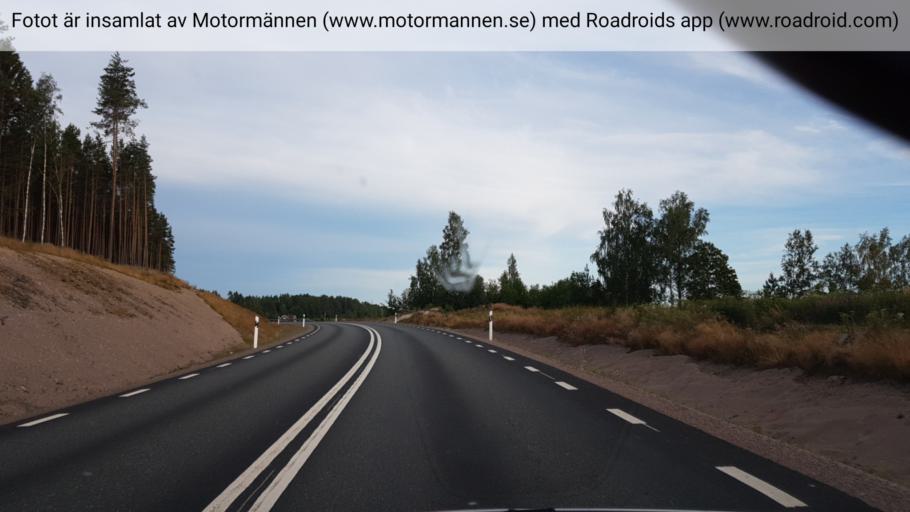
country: SE
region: Vaestra Goetaland
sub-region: Tibro Kommun
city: Tibro
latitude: 58.4548
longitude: 14.1779
